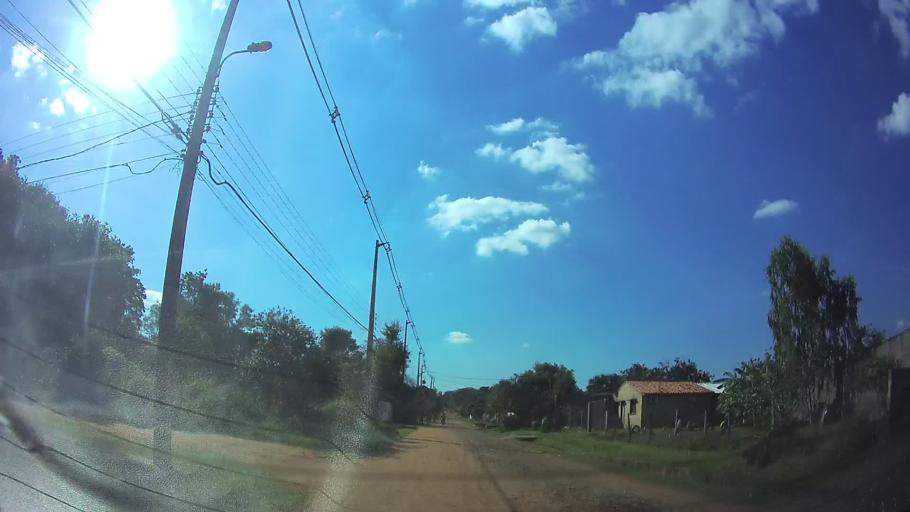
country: PY
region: Central
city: Limpio
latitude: -25.2556
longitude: -57.4750
